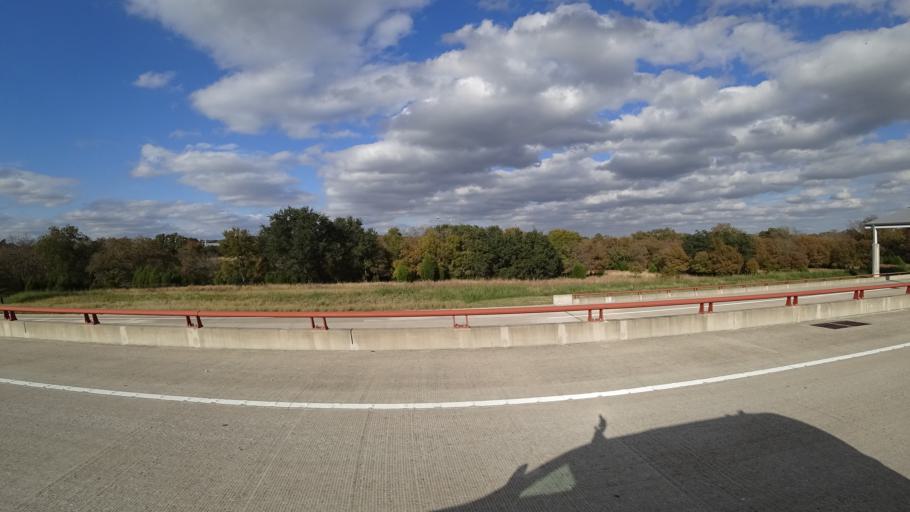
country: US
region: Texas
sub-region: Williamson County
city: Brushy Creek
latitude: 30.4797
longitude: -97.7356
